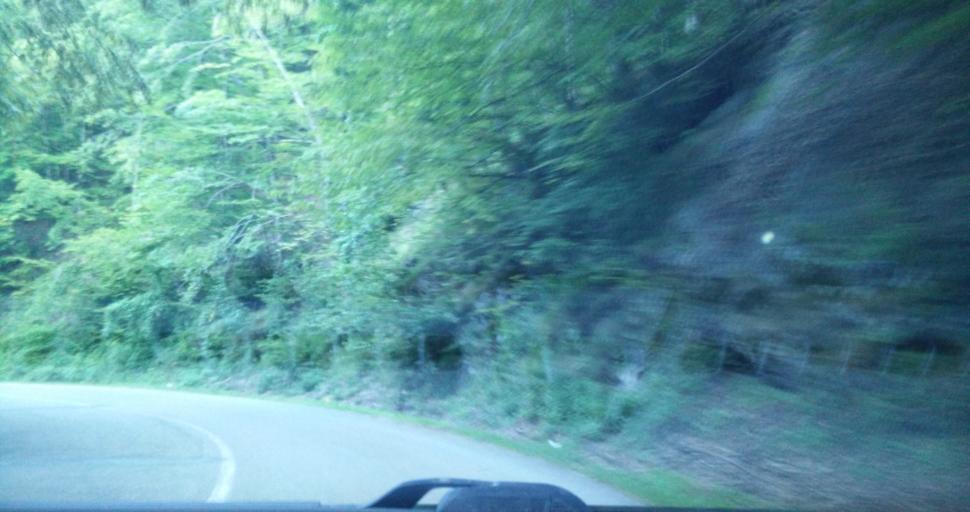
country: RO
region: Bihor
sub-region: Oras Nucet
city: Nucet
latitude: 46.4856
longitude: 22.6034
